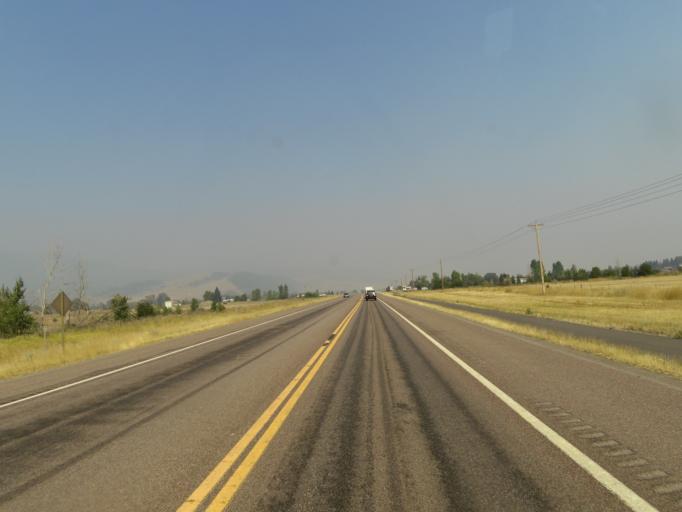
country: US
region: Montana
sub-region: Missoula County
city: Frenchtown
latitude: 47.1439
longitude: -114.0504
